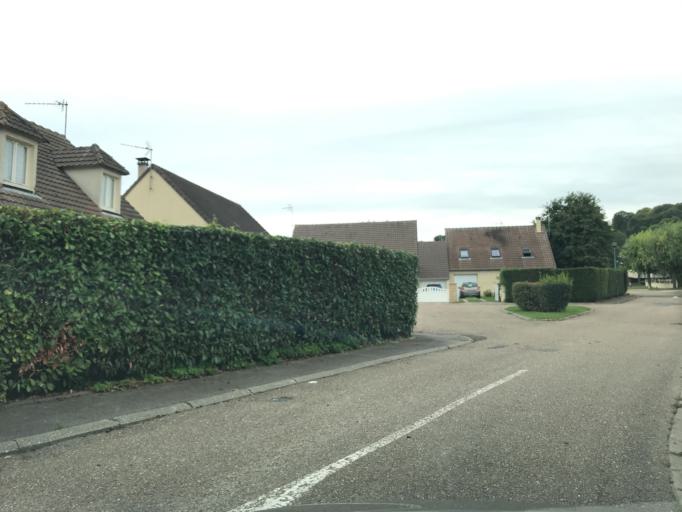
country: FR
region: Haute-Normandie
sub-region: Departement de l'Eure
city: Aubevoye
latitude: 49.1661
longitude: 1.3366
